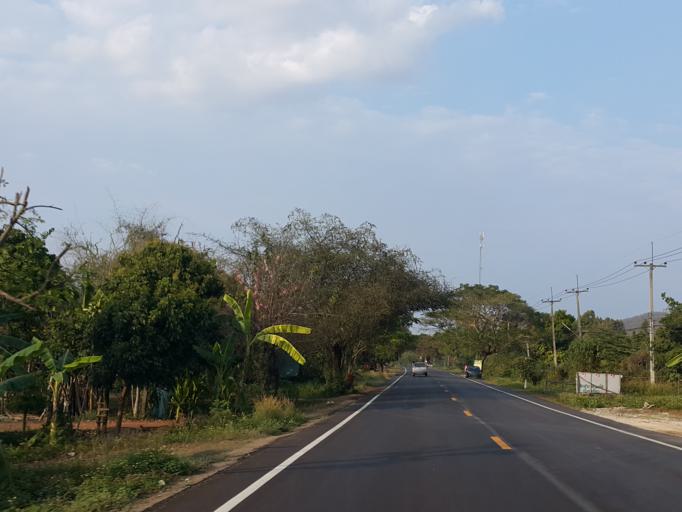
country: TH
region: Lampang
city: Lampang
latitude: 18.4769
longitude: 99.4687
